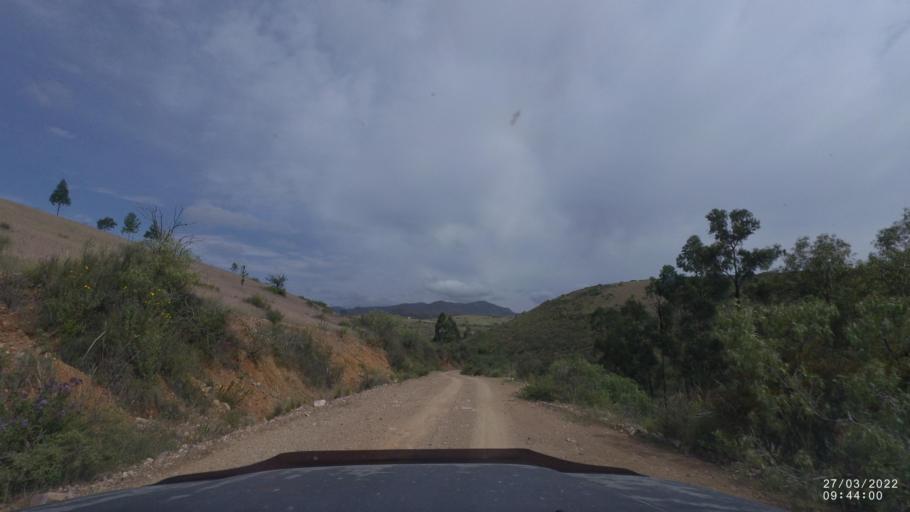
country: BO
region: Cochabamba
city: Cliza
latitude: -17.7499
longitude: -65.9083
